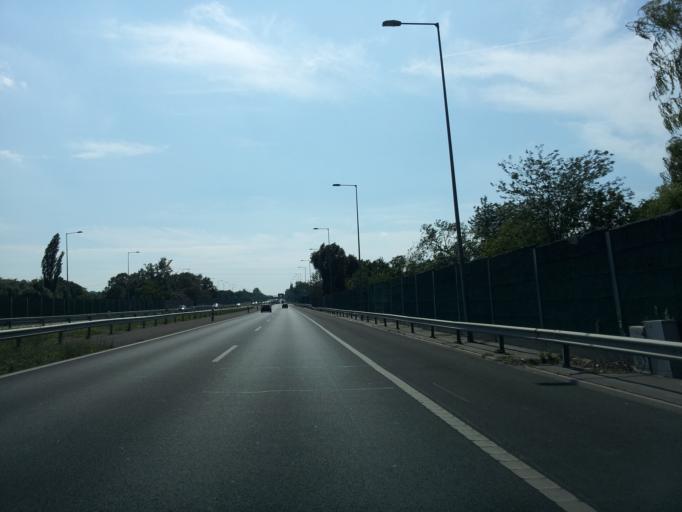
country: HU
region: Pest
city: Toeroekbalint
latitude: 47.4479
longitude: 18.9112
